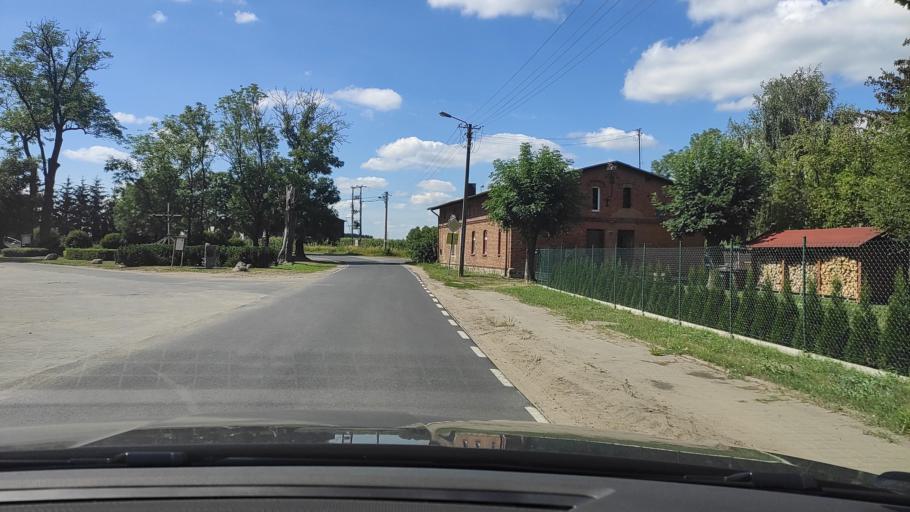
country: PL
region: Greater Poland Voivodeship
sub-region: Powiat poznanski
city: Kobylnica
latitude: 52.4843
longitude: 17.1555
